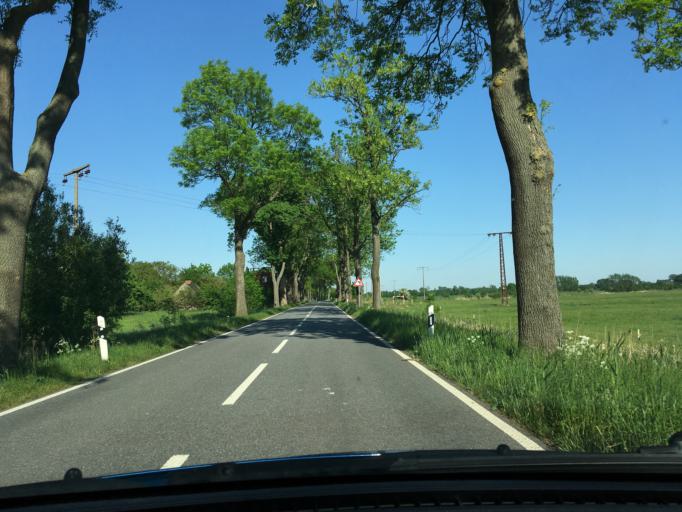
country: DE
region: Brandenburg
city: Lenzen
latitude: 53.0845
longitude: 11.4455
